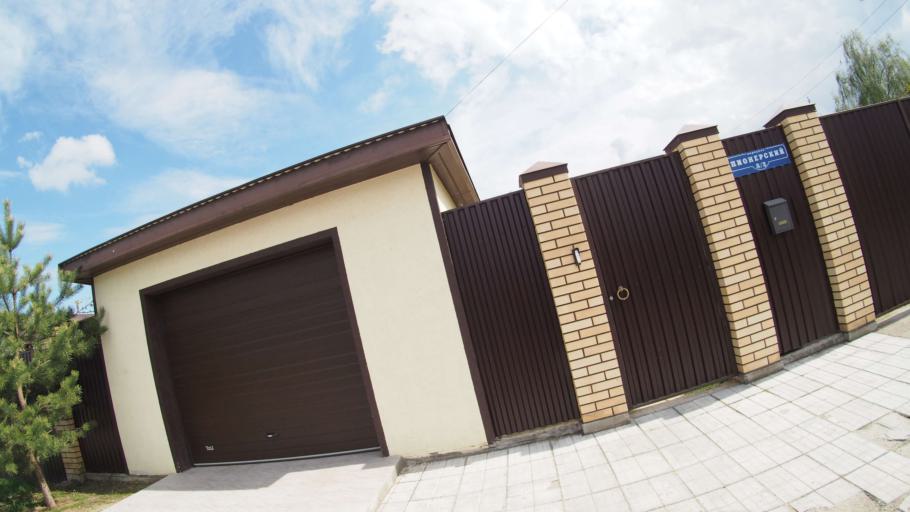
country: RU
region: Moskovskaya
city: Ramenskoye
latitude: 55.5579
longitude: 38.2397
